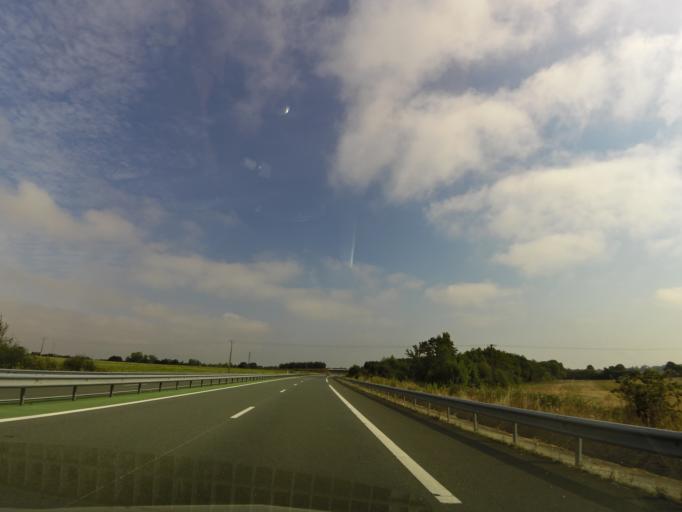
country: FR
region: Pays de la Loire
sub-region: Departement de la Vendee
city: Les Essarts
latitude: 46.7659
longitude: -1.2683
